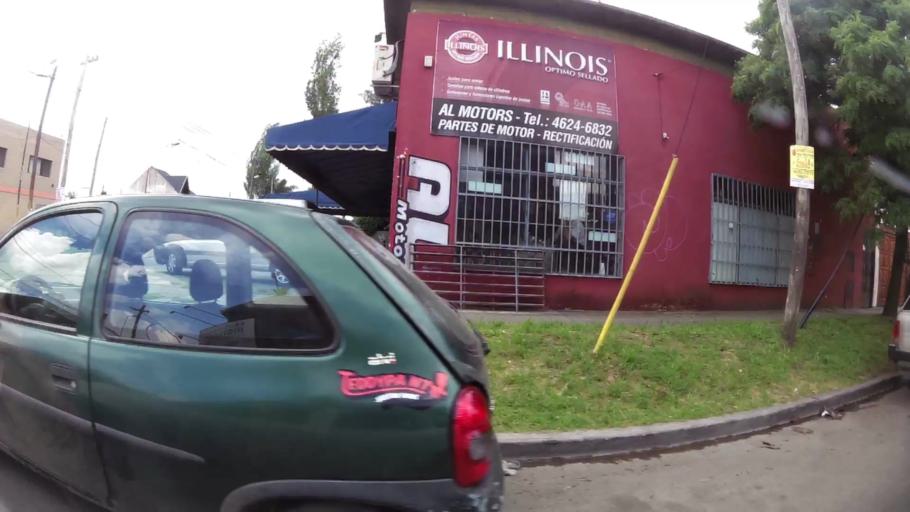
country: AR
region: Buenos Aires
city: Ituzaingo
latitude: -34.6404
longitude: -58.6751
